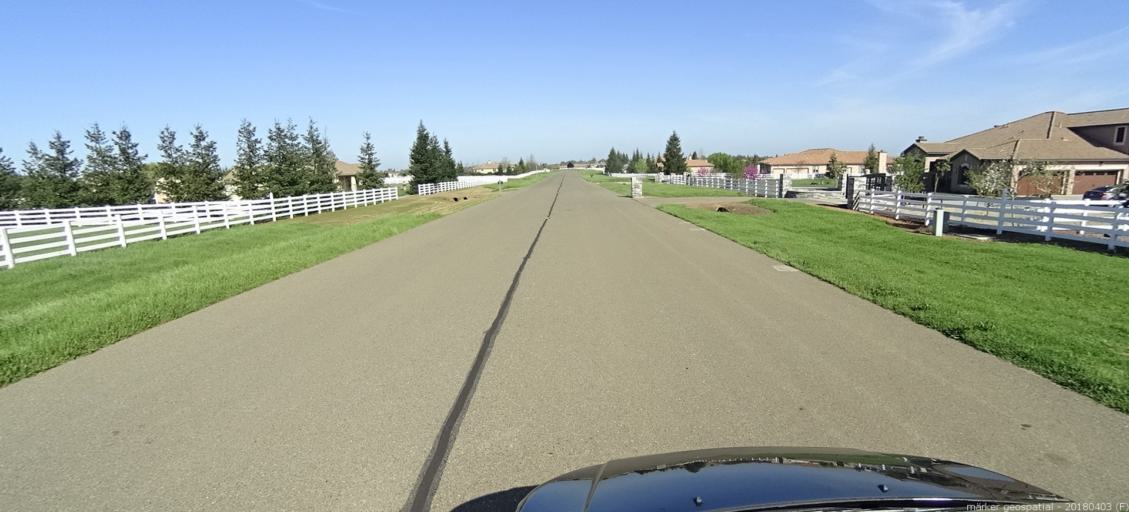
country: US
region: California
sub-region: Sacramento County
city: Wilton
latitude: 38.4083
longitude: -121.1956
